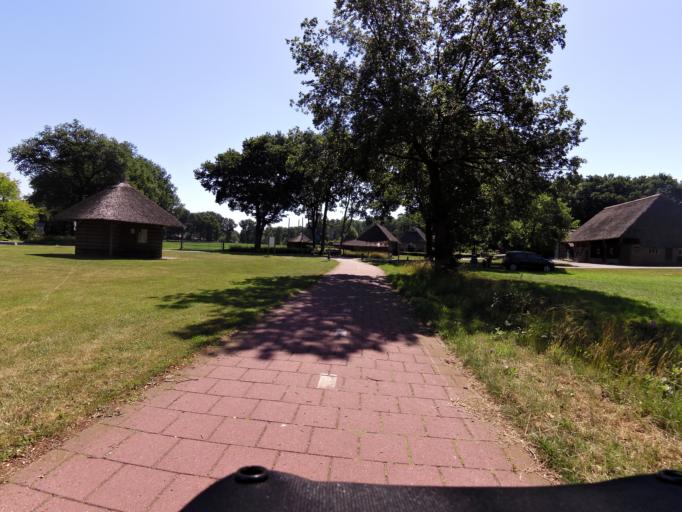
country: NL
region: Overijssel
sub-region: Gemeente Twenterand
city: Magele
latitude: 52.5124
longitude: 6.5320
